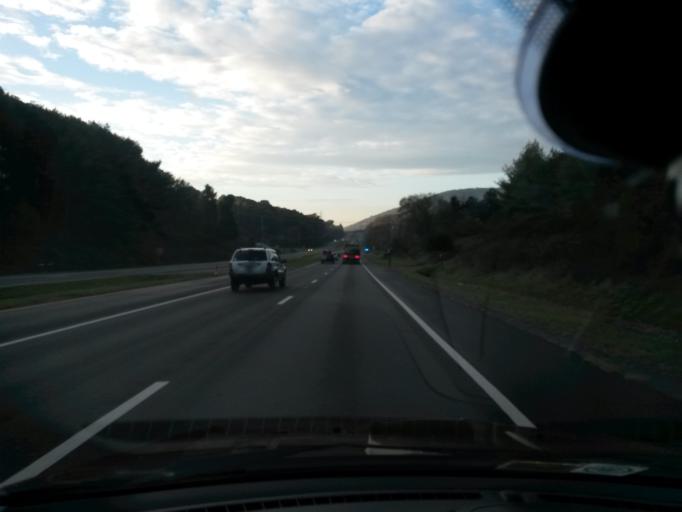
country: US
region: Virginia
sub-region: Botetourt County
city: Cloverdale
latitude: 37.3739
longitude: -79.8865
